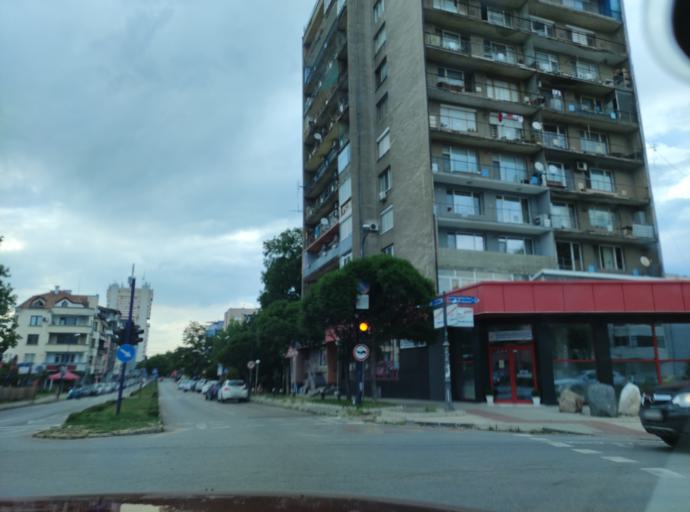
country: BG
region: Pazardzhik
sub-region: Obshtina Pazardzhik
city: Pazardzhik
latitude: 42.1863
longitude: 24.3346
